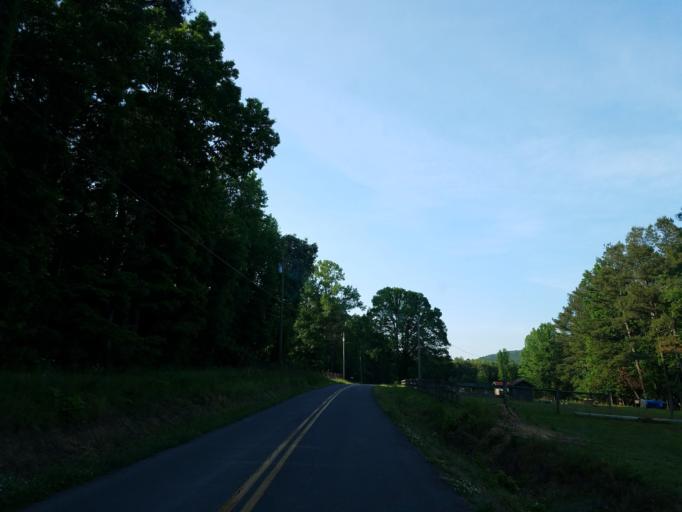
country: US
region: Georgia
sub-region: Gordon County
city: Calhoun
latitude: 34.5529
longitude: -85.1057
